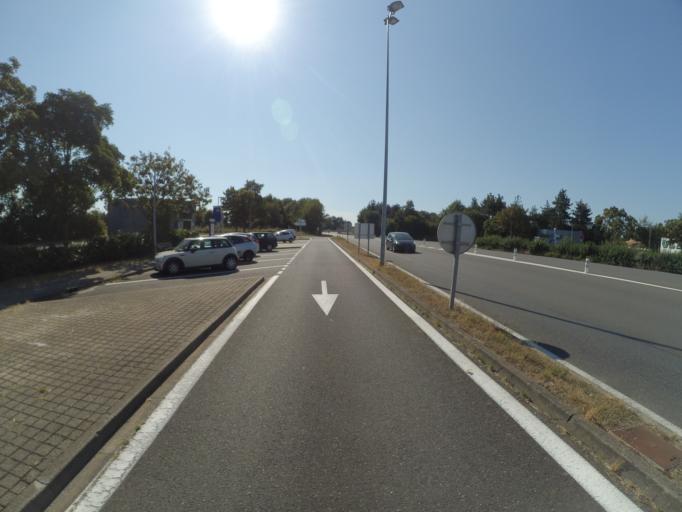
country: FR
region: Pays de la Loire
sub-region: Departement de la Vendee
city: Bouffere
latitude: 46.9592
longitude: -1.3519
